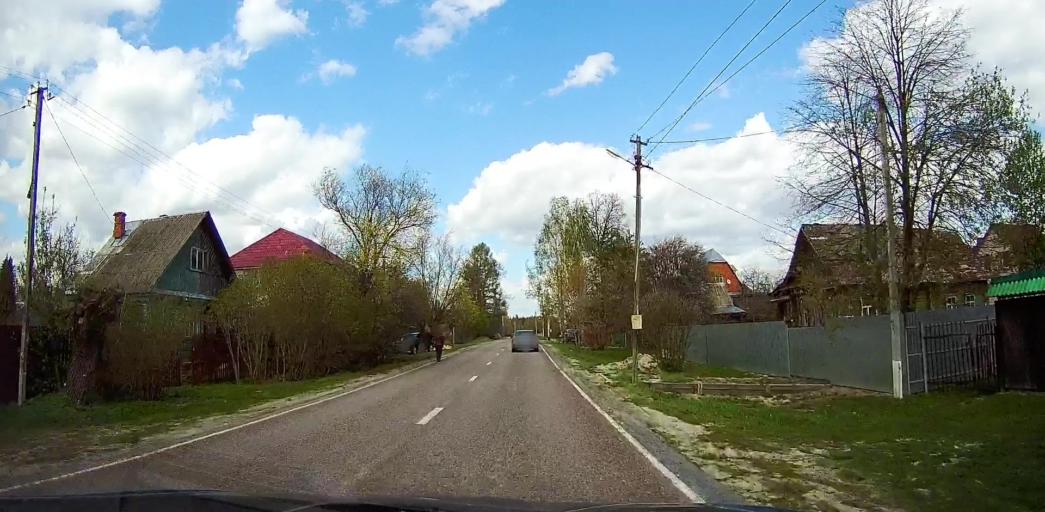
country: RU
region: Moskovskaya
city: Davydovo
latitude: 55.5847
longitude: 38.8276
